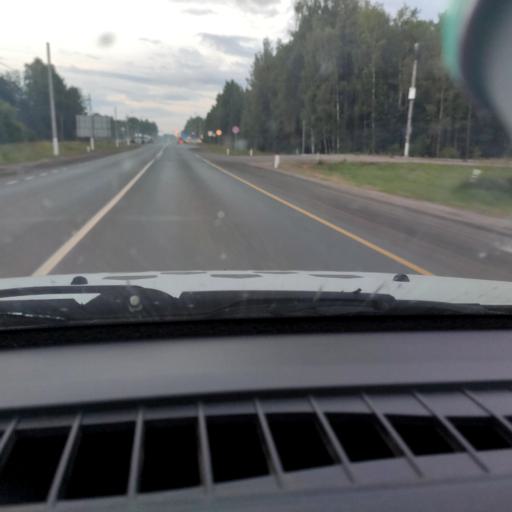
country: RU
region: Kirov
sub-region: Kirovo-Chepetskiy Rayon
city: Kirov
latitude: 58.6824
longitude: 49.6428
